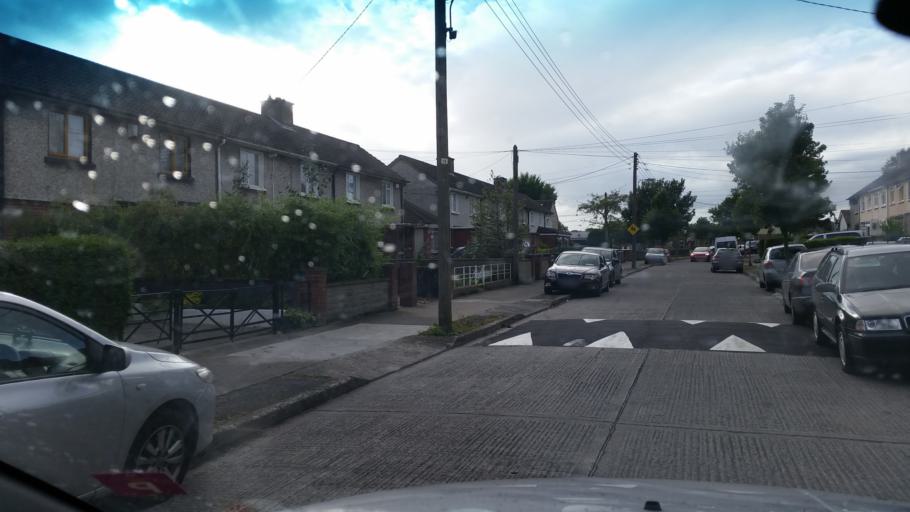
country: IE
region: Leinster
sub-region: Dublin City
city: Finglas
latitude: 53.3873
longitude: -6.2851
